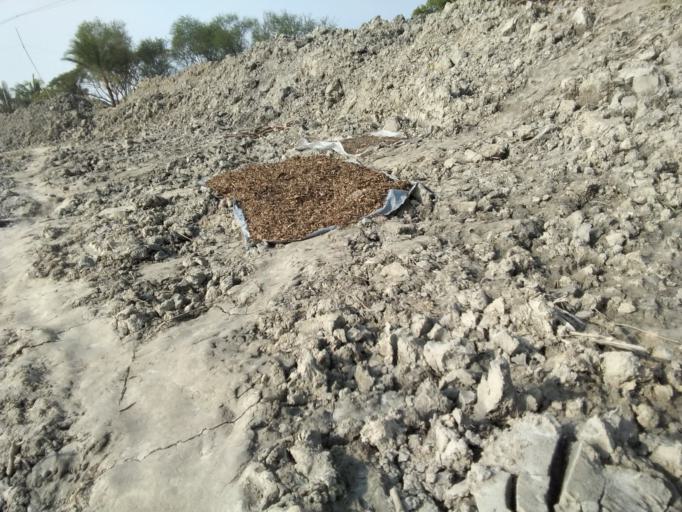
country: IN
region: West Bengal
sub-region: North 24 Parganas
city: Taki
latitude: 22.5918
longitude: 89.0339
